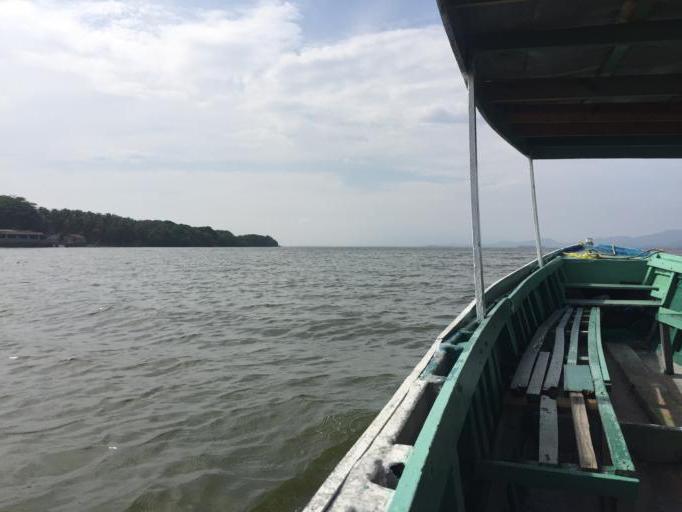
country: MX
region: Guerrero
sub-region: Coyuca de Benitez
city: Colonia Luces en el Mar
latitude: 16.9106
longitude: -99.9761
